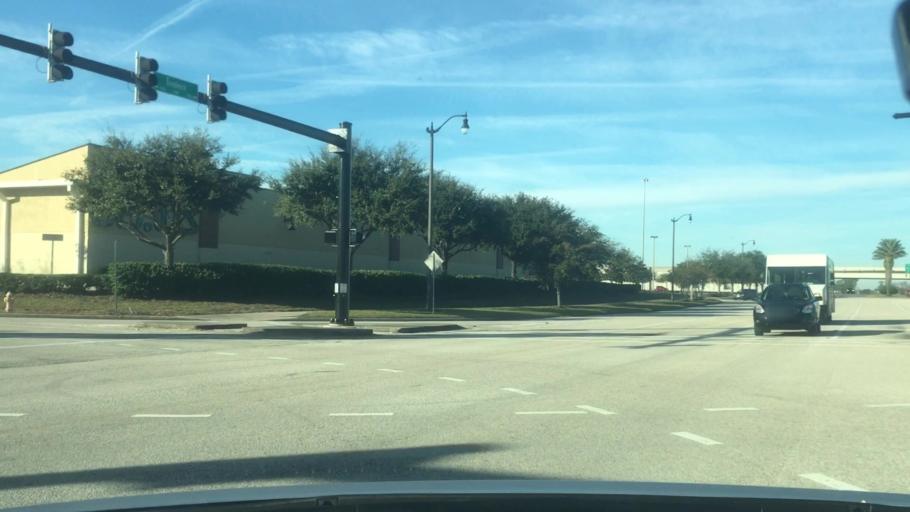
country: US
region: Florida
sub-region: Duval County
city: Jacksonville
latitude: 30.3380
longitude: -81.5489
